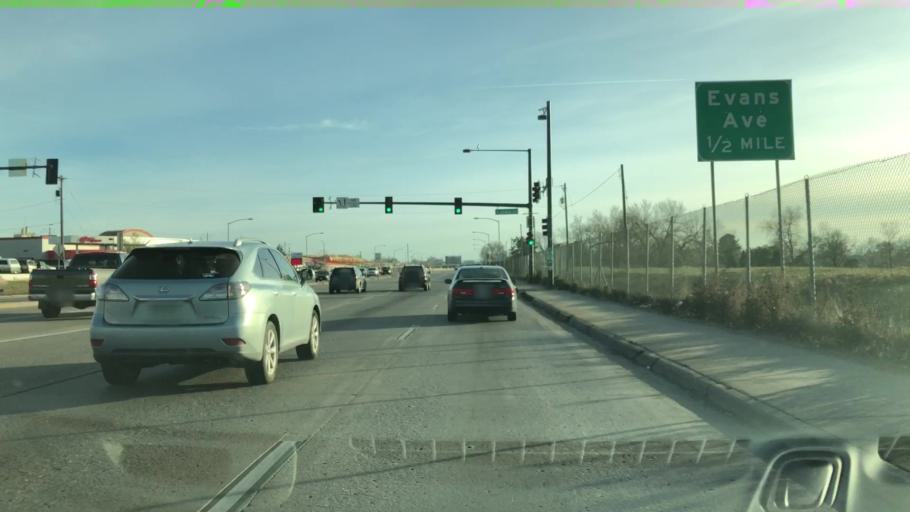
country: US
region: Colorado
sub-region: Arapahoe County
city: Englewood
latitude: 39.6880
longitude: -104.9922
